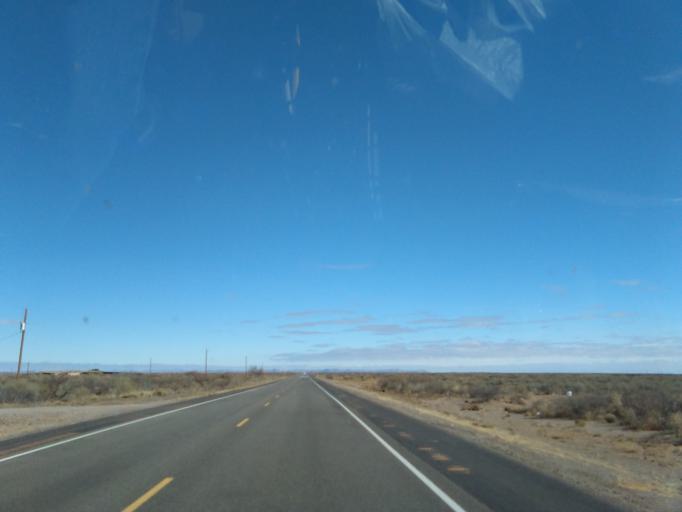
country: US
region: New Mexico
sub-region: Luna County
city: Deming
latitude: 32.2963
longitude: -107.7253
